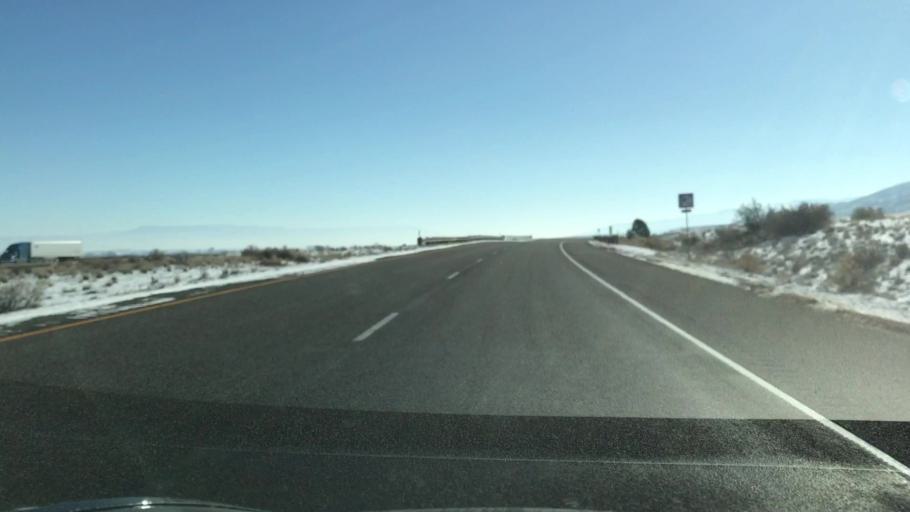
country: US
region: Colorado
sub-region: Mesa County
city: Loma
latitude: 39.2144
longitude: -108.8696
